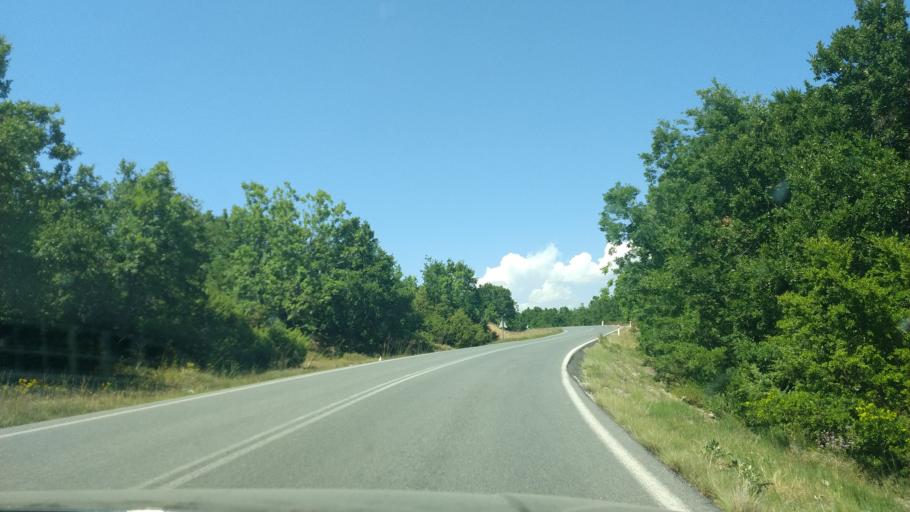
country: GR
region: West Macedonia
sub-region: Nomos Grevenon
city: Grevena
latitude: 40.0157
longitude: 21.4869
